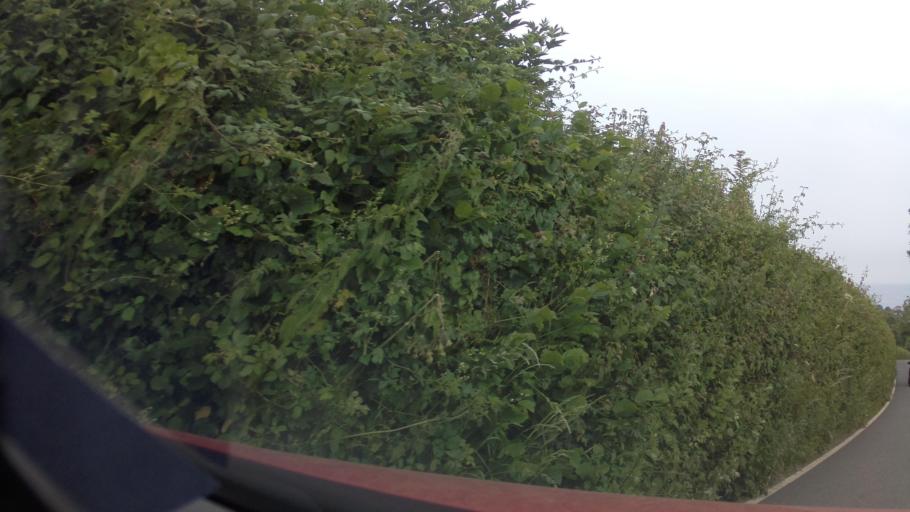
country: GB
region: England
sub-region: Devon
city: Colyton
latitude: 50.7060
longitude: -3.1010
